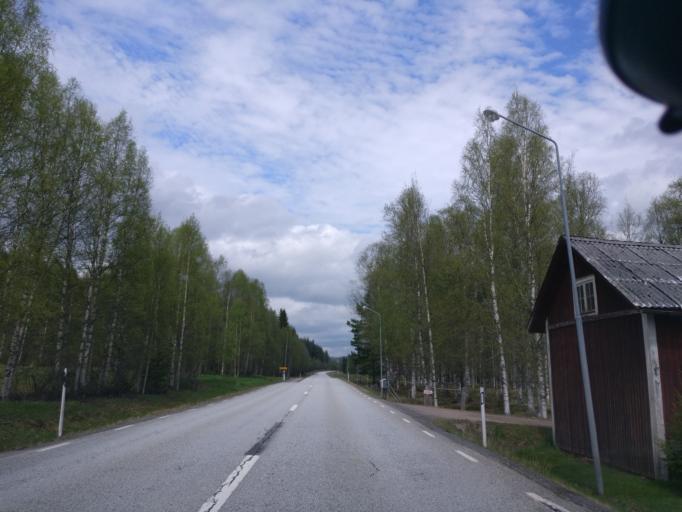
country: SE
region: Vaermland
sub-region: Hagfors Kommun
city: Ekshaerad
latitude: 60.1164
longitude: 13.5382
